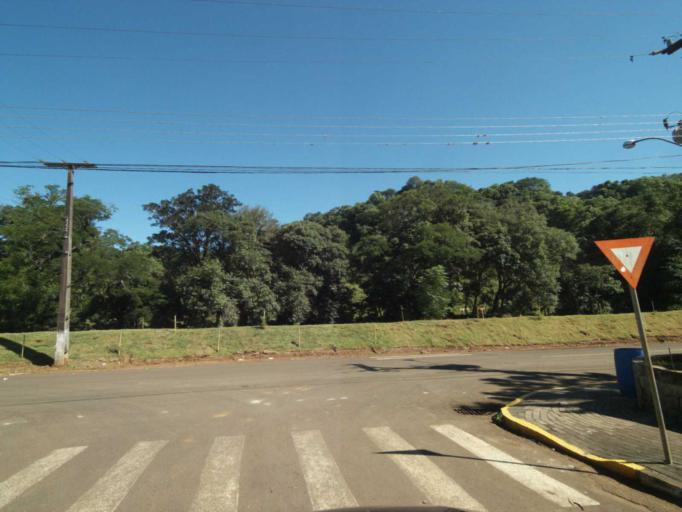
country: BR
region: Parana
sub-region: Francisco Beltrao
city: Francisco Beltrao
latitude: -26.1433
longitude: -53.3120
